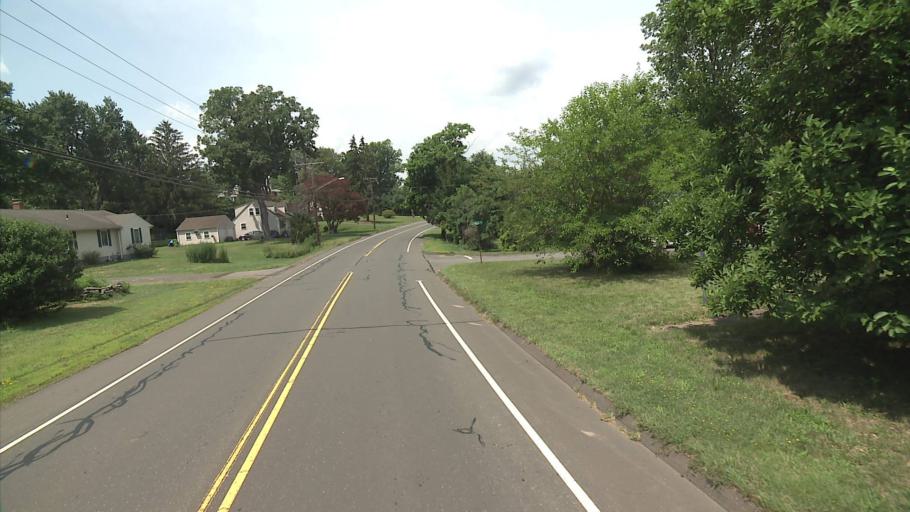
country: US
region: Connecticut
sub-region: Middlesex County
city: Middletown
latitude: 41.5325
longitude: -72.6442
